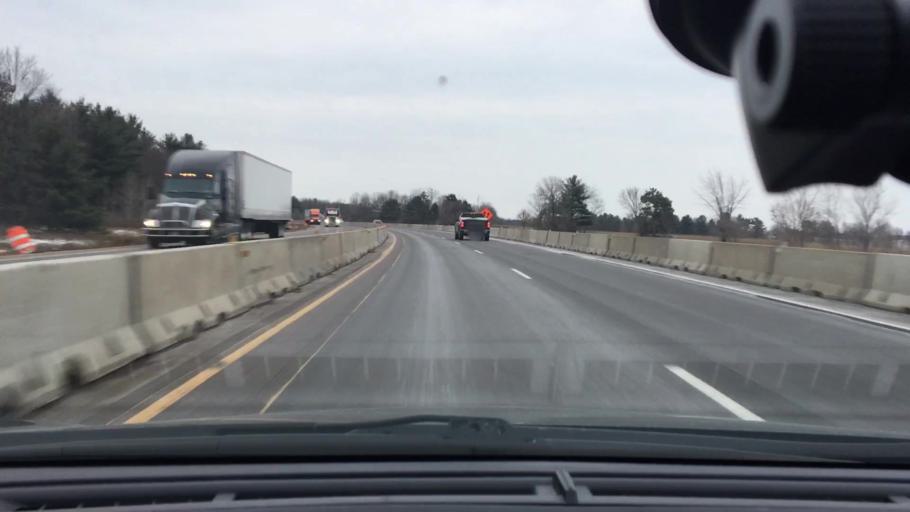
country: US
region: Wisconsin
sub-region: Dunn County
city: Menomonie
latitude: 44.9082
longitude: -91.9605
